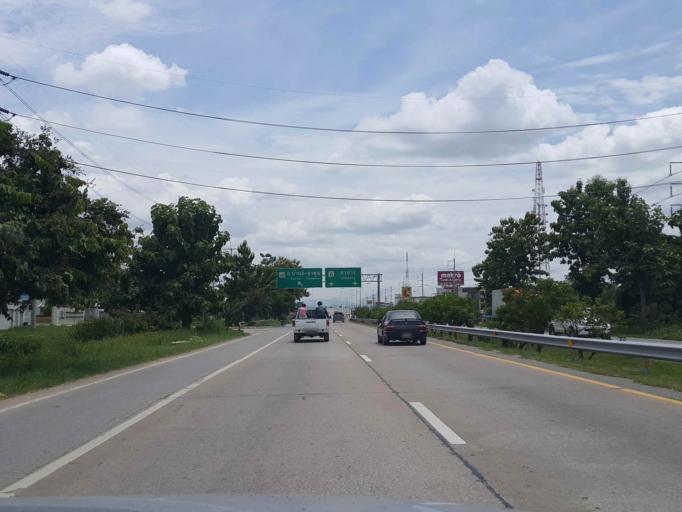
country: TH
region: Lamphun
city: Lamphun
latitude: 18.5955
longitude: 99.0428
